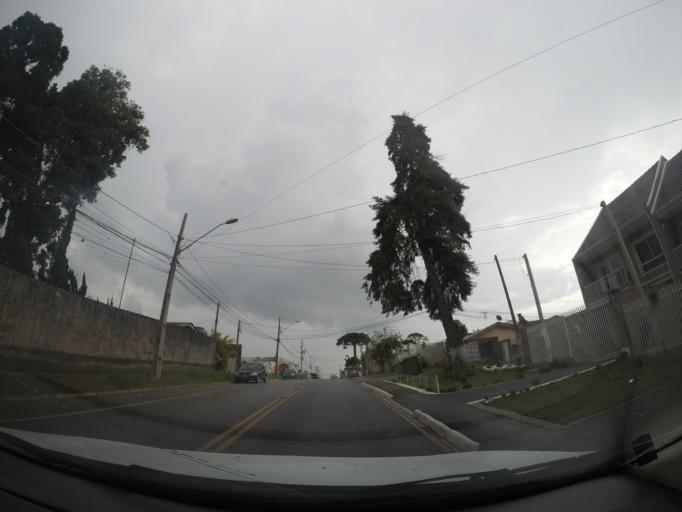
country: BR
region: Parana
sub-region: Sao Jose Dos Pinhais
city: Sao Jose dos Pinhais
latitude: -25.5177
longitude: -49.2536
